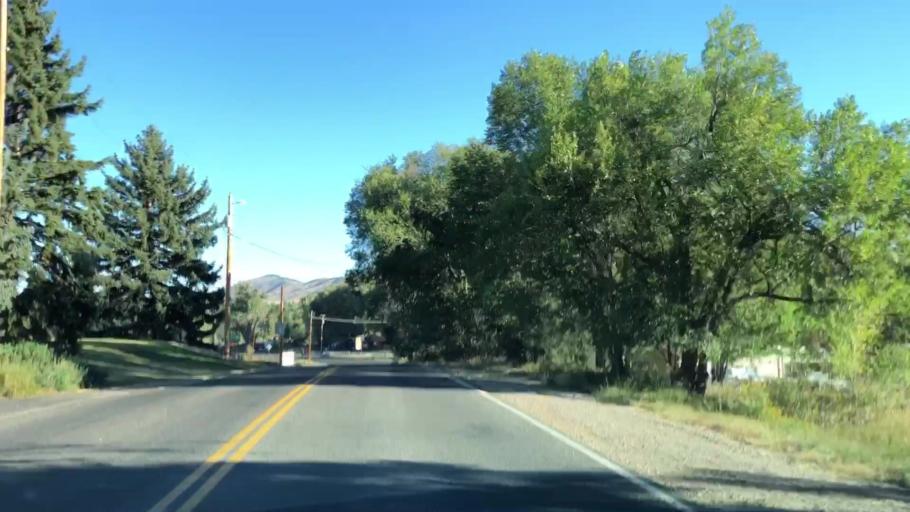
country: US
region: Colorado
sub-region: Larimer County
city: Loveland
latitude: 40.4114
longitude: -105.1688
